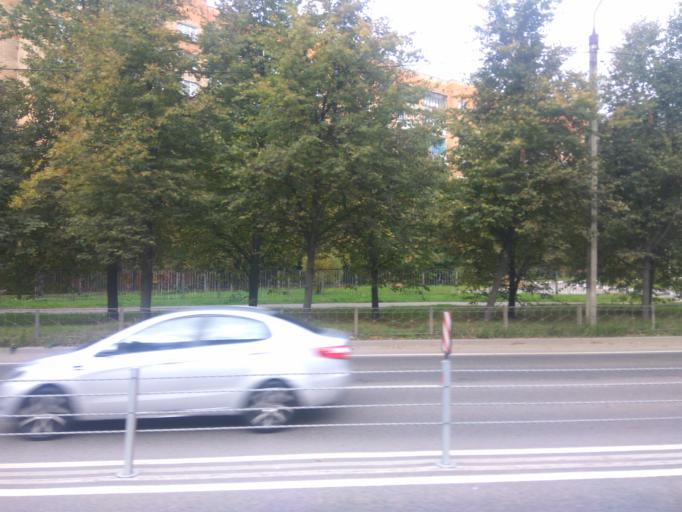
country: RU
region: Moskovskaya
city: Fryazino
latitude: 55.9509
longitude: 38.0501
